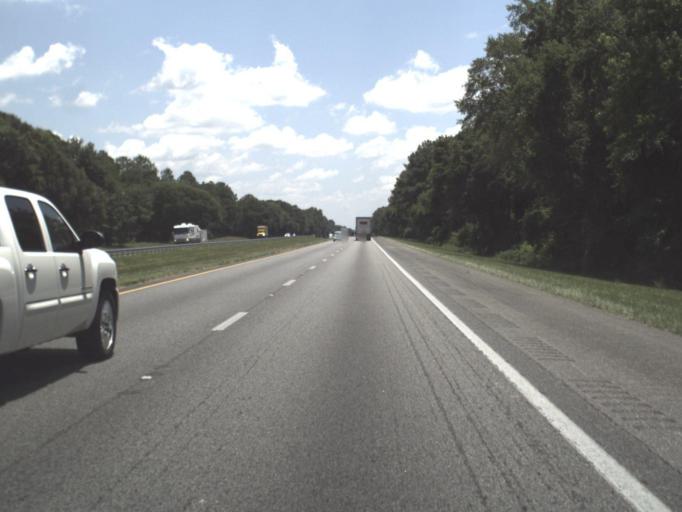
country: US
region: Florida
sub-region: Madison County
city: Madison
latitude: 30.4314
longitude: -83.6076
